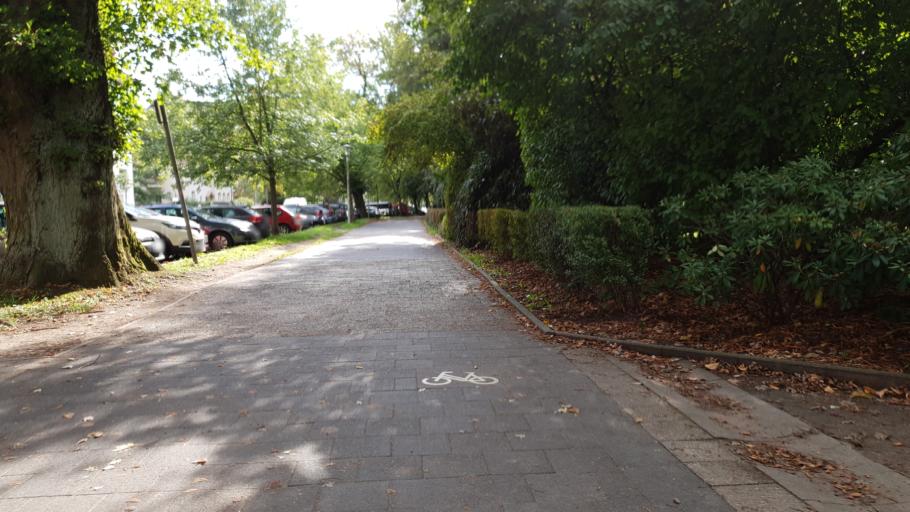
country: DE
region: Schleswig-Holstein
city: Kiel
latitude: 54.3274
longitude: 10.1257
